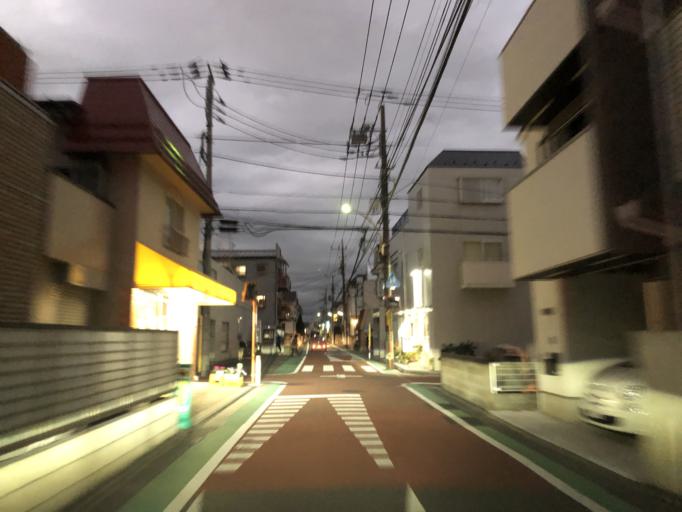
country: JP
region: Tokyo
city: Kokubunji
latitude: 35.7099
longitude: 139.4409
